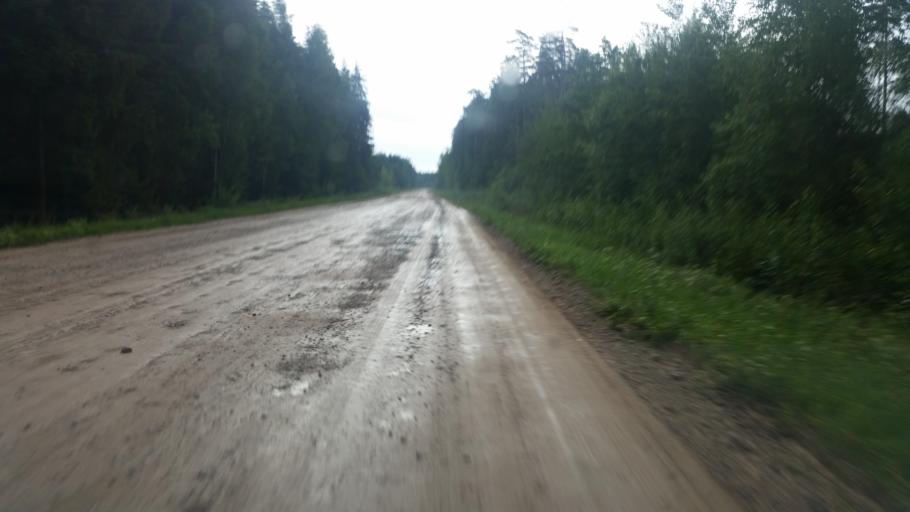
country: LV
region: Vecumnieki
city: Vecumnieki
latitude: 56.4284
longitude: 24.5437
